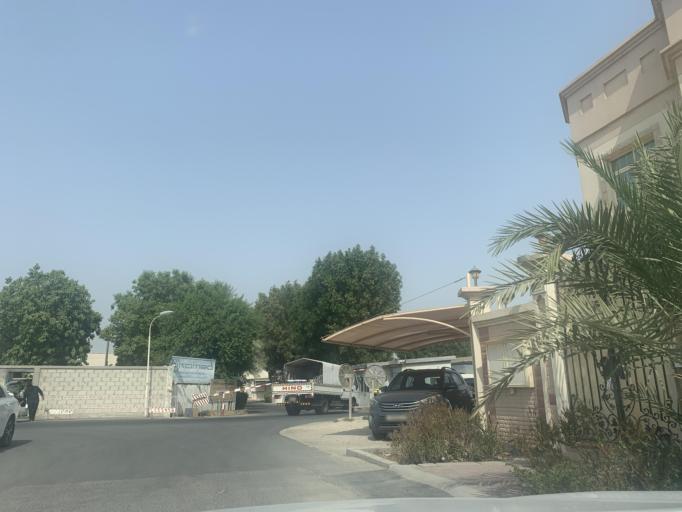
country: BH
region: Manama
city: Jidd Hafs
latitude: 26.2209
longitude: 50.4728
